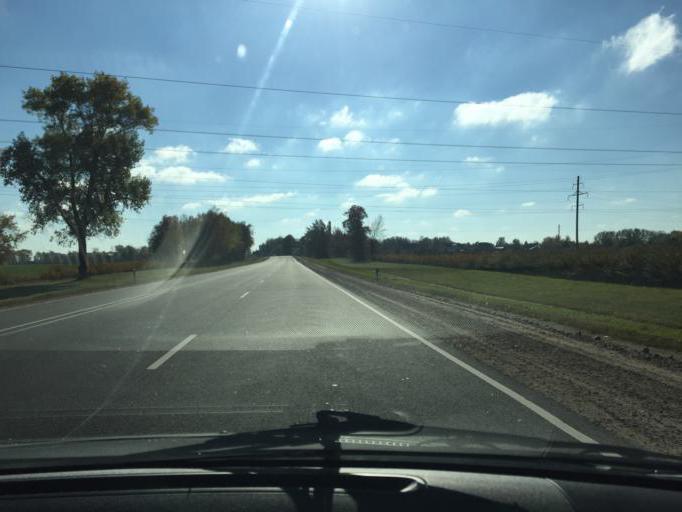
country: BY
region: Minsk
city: Slutsk
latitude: 53.0587
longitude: 27.5536
